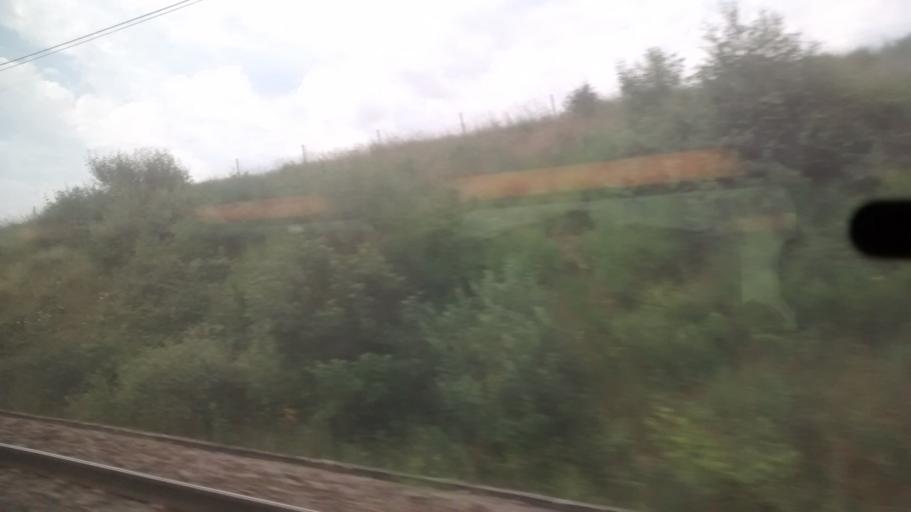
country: FR
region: Bourgogne
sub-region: Departement de la Cote-d'Or
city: Saulieu
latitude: 47.2415
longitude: 4.2964
